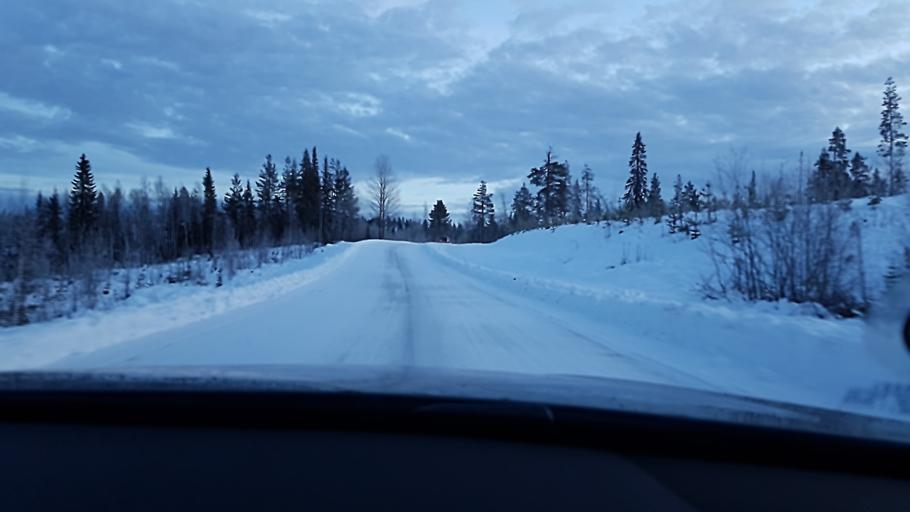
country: SE
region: Vaesterbotten
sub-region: Sorsele Kommun
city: Sorsele
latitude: 65.5026
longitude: 17.5498
